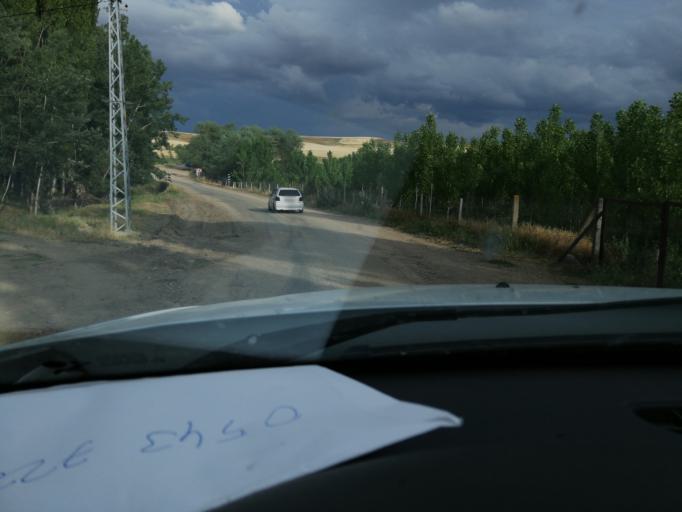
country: TR
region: Kirsehir
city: Kirsehir
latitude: 39.0284
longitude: 34.1298
